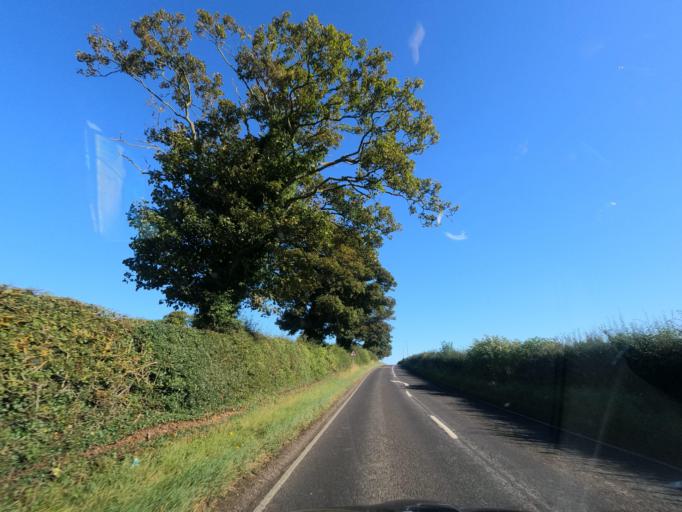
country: GB
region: England
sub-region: Northumberland
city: Ford
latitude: 55.7287
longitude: -2.0945
